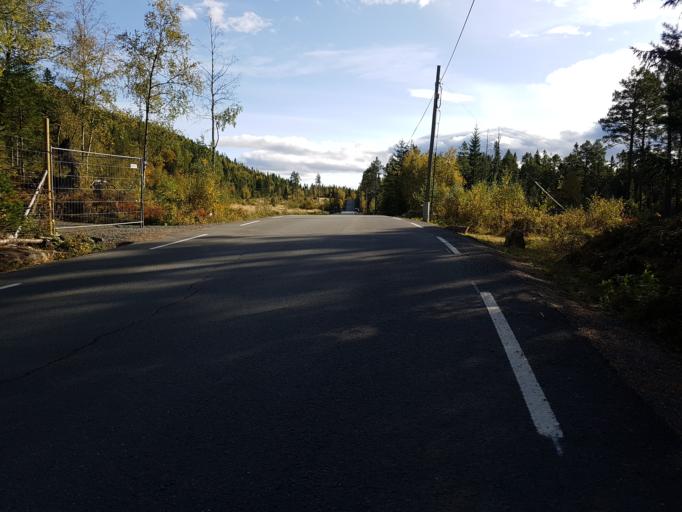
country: NO
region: Sor-Trondelag
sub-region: Malvik
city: Malvik
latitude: 63.3736
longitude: 10.6118
